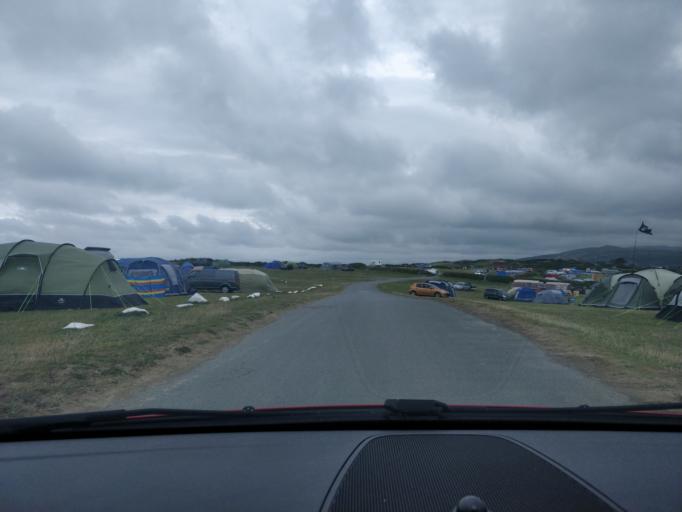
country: GB
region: Wales
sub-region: Gwynedd
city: Llanfair
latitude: 52.8136
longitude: -4.1507
